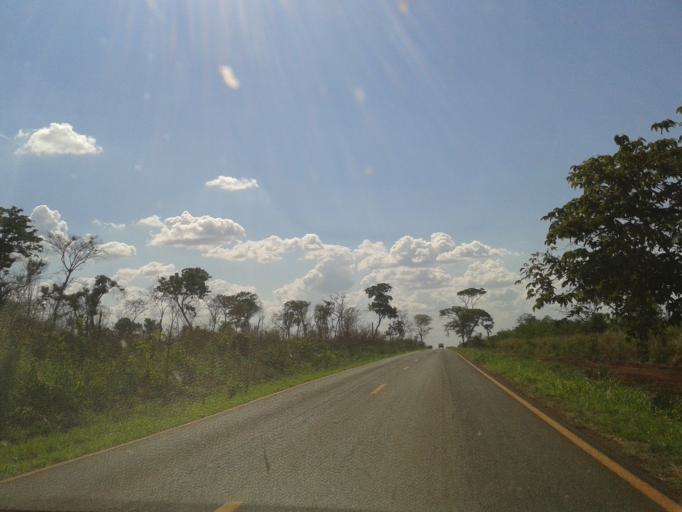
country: BR
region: Minas Gerais
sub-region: Centralina
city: Centralina
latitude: -18.6959
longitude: -49.3276
